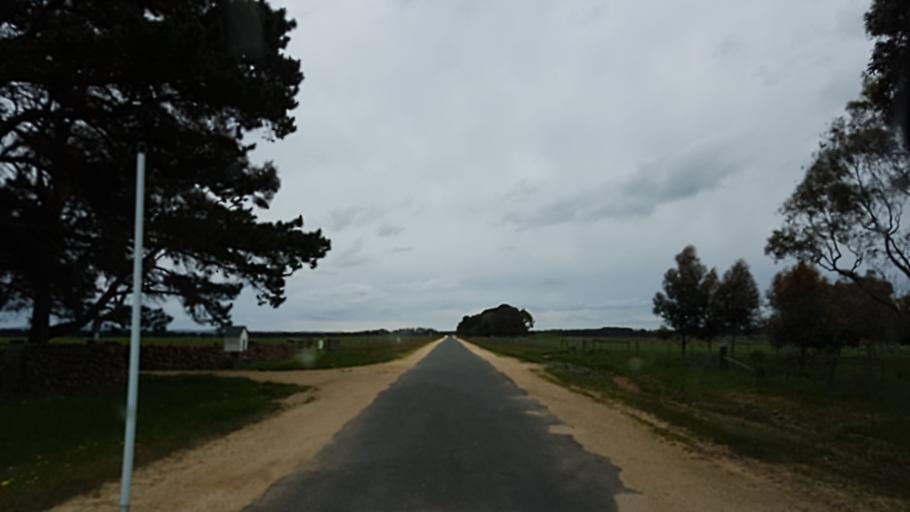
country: AU
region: Victoria
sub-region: Moorabool
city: Bacchus Marsh
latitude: -37.7494
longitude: 144.1560
